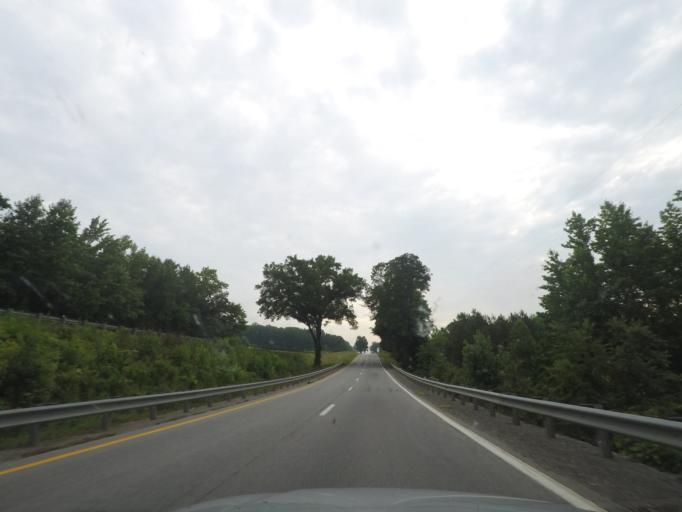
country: US
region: Virginia
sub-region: Mecklenburg County
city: Chase City
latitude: 36.8956
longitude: -78.5436
